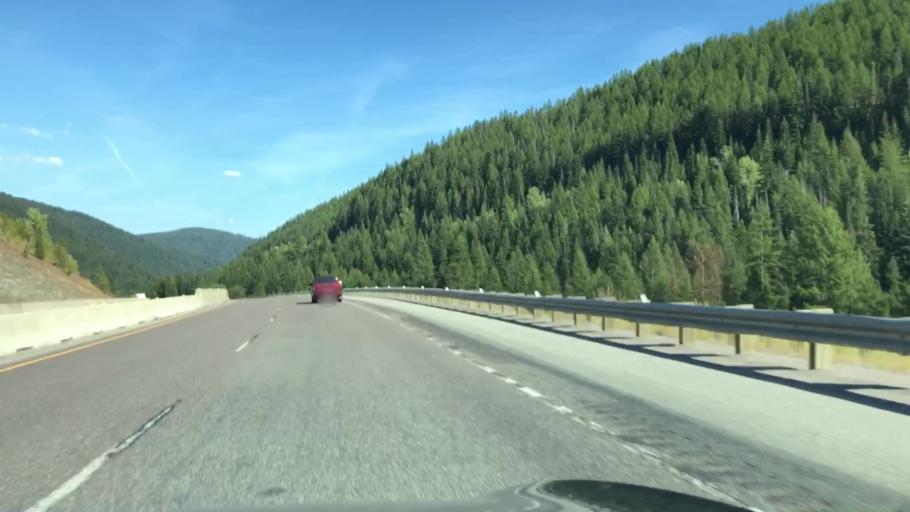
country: US
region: Montana
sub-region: Sanders County
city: Thompson Falls
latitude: 47.4156
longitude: -115.5754
